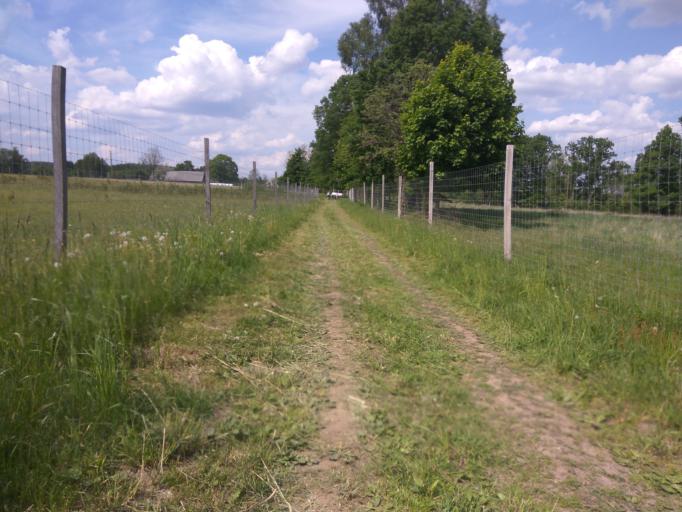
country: LV
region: Kuldigas Rajons
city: Kuldiga
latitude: 56.8899
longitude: 21.9300
